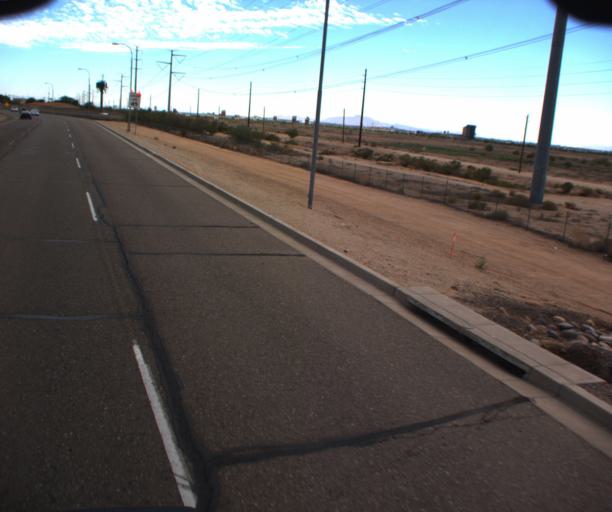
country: US
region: Arizona
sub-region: Maricopa County
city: Guadalupe
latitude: 33.2914
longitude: -111.9905
